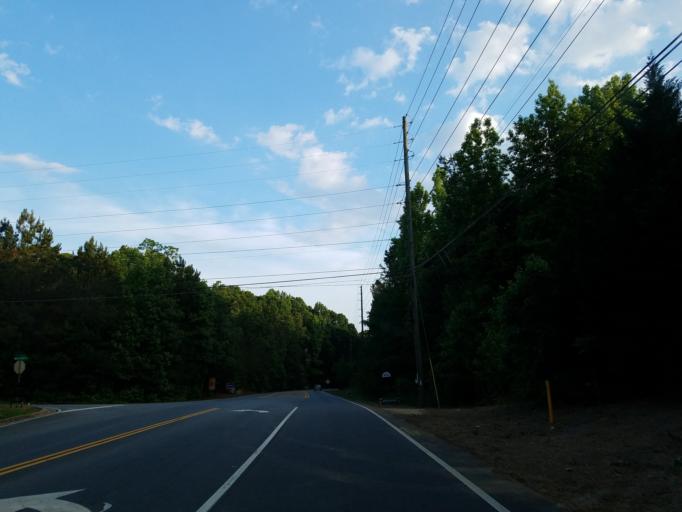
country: US
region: Georgia
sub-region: Cherokee County
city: Holly Springs
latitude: 34.1869
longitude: -84.5432
